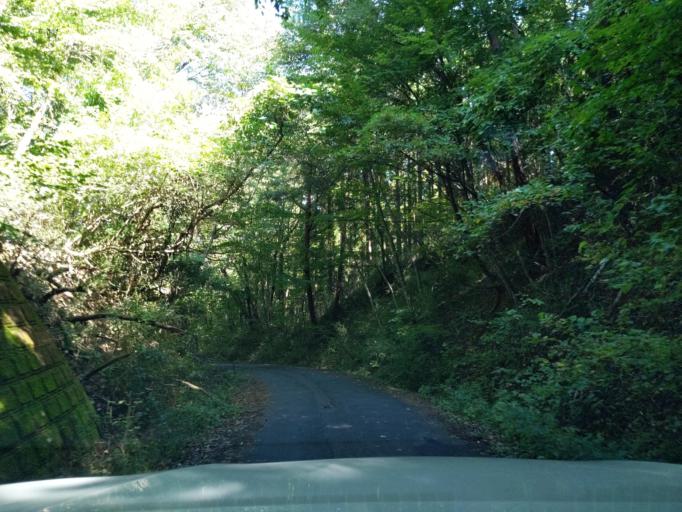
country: JP
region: Fukushima
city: Koriyama
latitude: 37.4010
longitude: 140.2391
